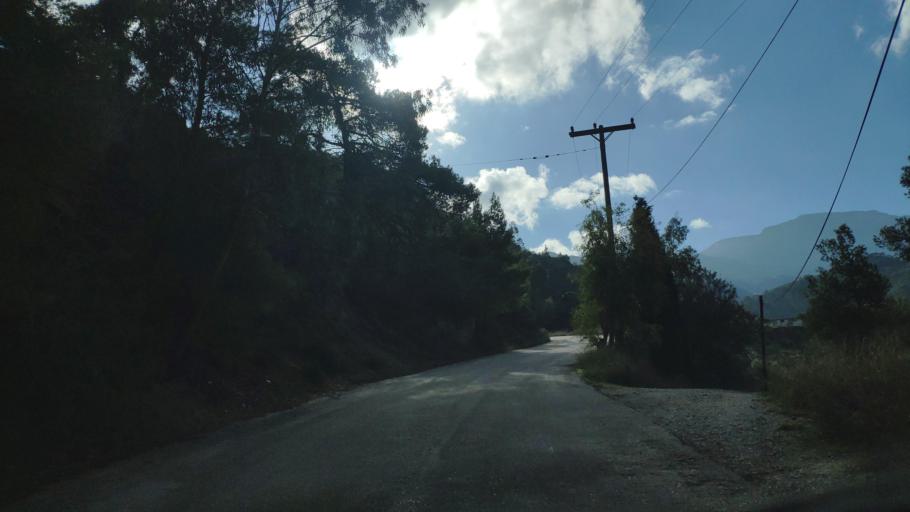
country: GR
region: West Greece
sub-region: Nomos Achaias
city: Aiyira
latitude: 38.1253
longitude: 22.4352
